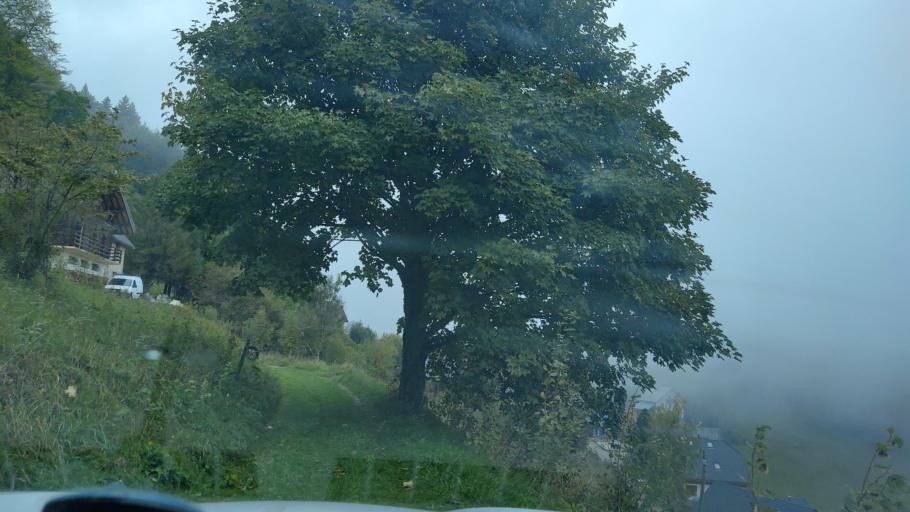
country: FR
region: Rhone-Alpes
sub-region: Departement de la Savoie
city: Les Echelles
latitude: 45.4119
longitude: 5.8397
